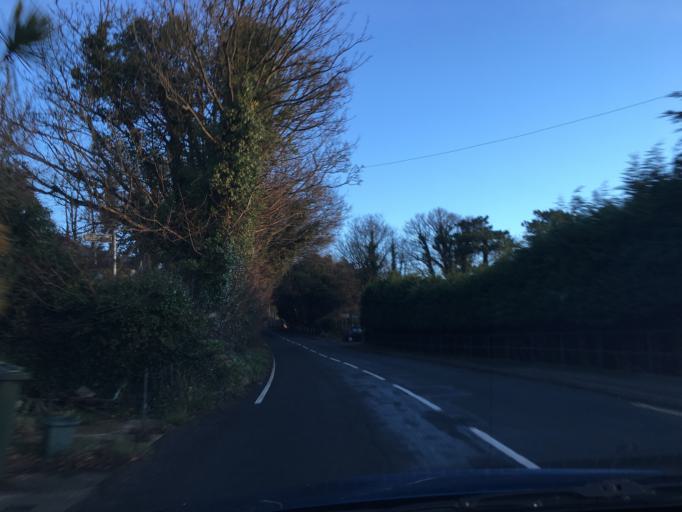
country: GB
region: England
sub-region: Isle of Wight
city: Shanklin
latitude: 50.6044
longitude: -1.1823
